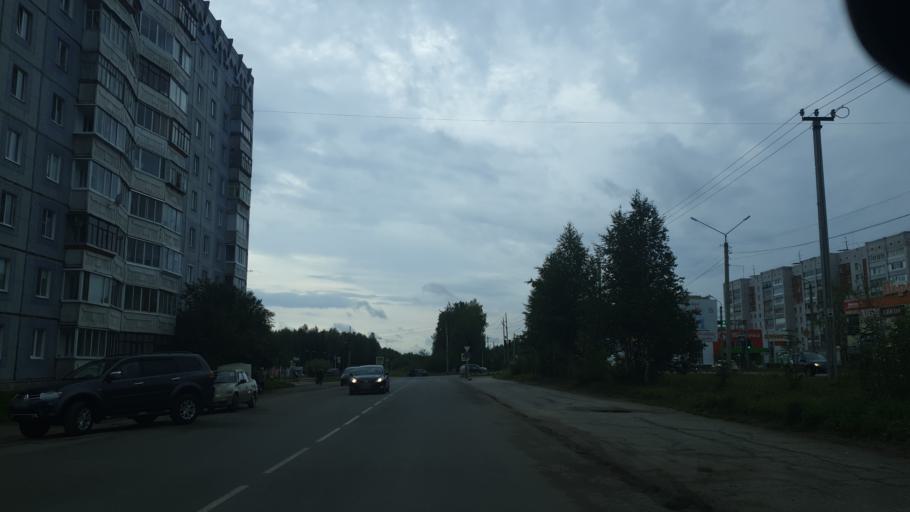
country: RU
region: Komi Republic
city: Ezhva
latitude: 61.7824
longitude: 50.7479
